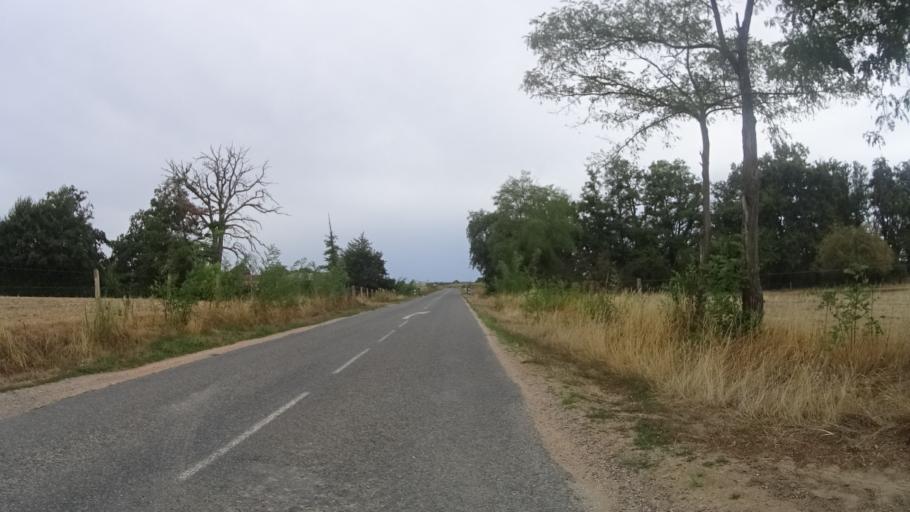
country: FR
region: Bourgogne
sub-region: Departement de la Nievre
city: Lucenay-les-Aix
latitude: 46.7732
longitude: 3.5497
